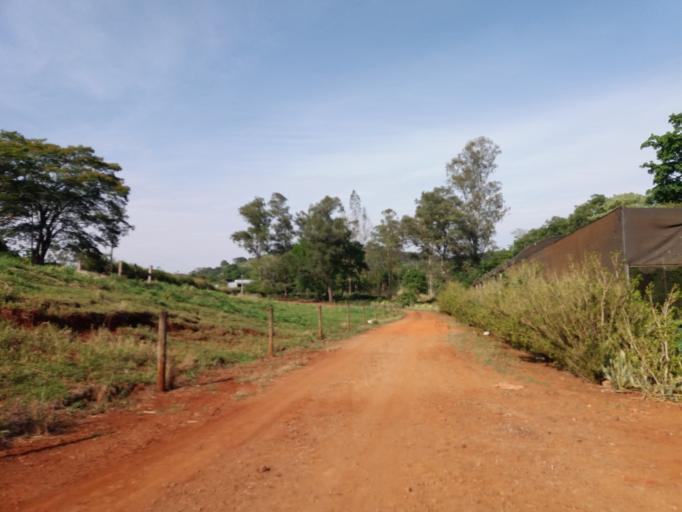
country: BR
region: Parana
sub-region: Londrina
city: Londrina
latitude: -23.5069
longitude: -51.1120
